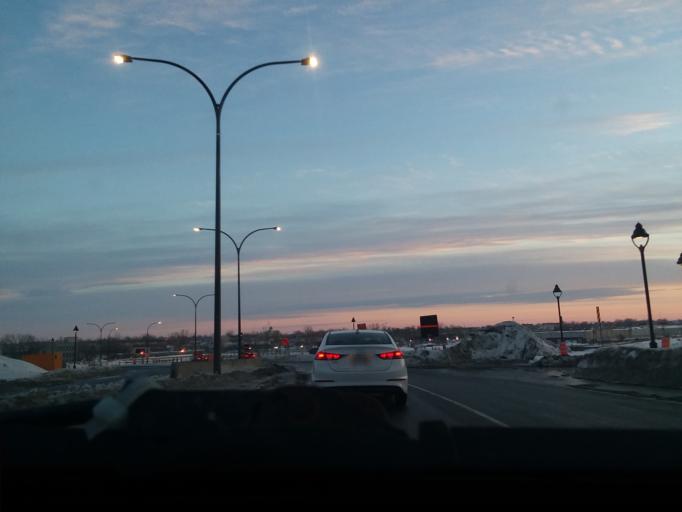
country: CA
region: Quebec
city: Montreal-Ouest
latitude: 45.4524
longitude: -73.6338
